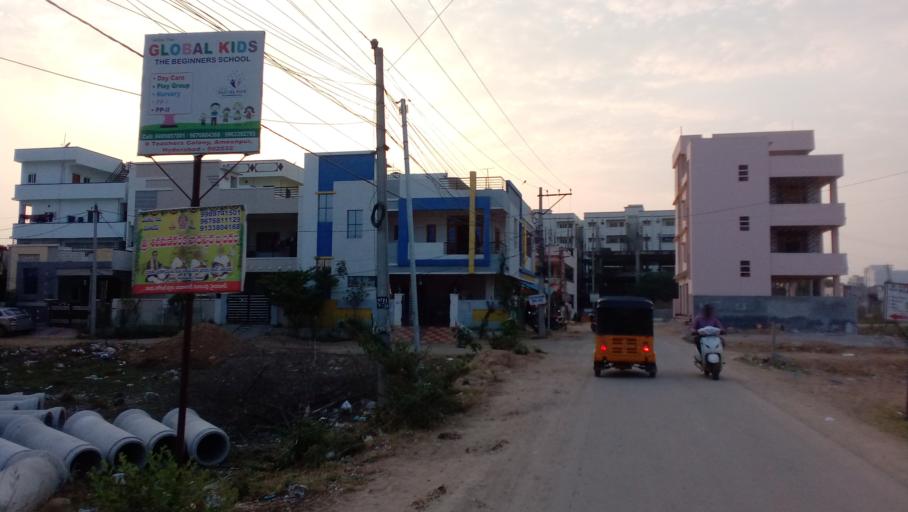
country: IN
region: Telangana
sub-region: Medak
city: Serilingampalle
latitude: 17.5175
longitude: 78.3154
